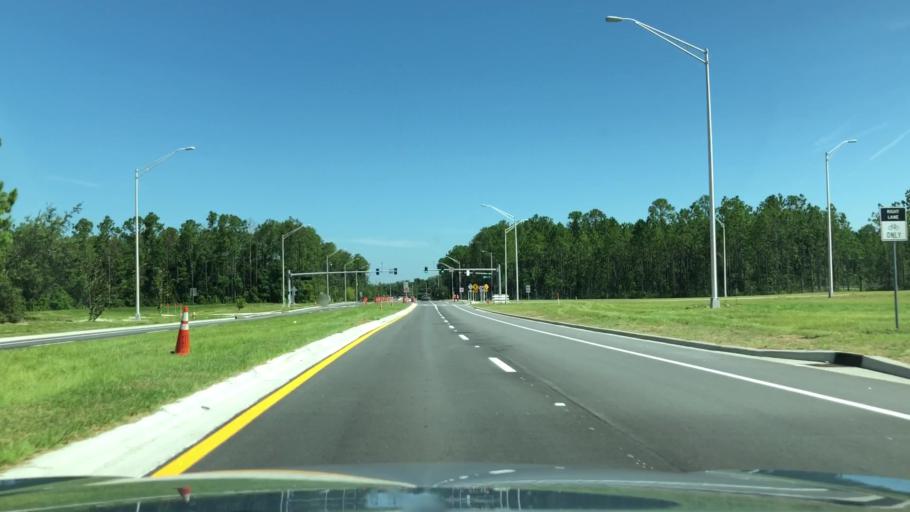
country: US
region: Florida
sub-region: Saint Johns County
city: Fruit Cove
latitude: 30.0796
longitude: -81.5320
